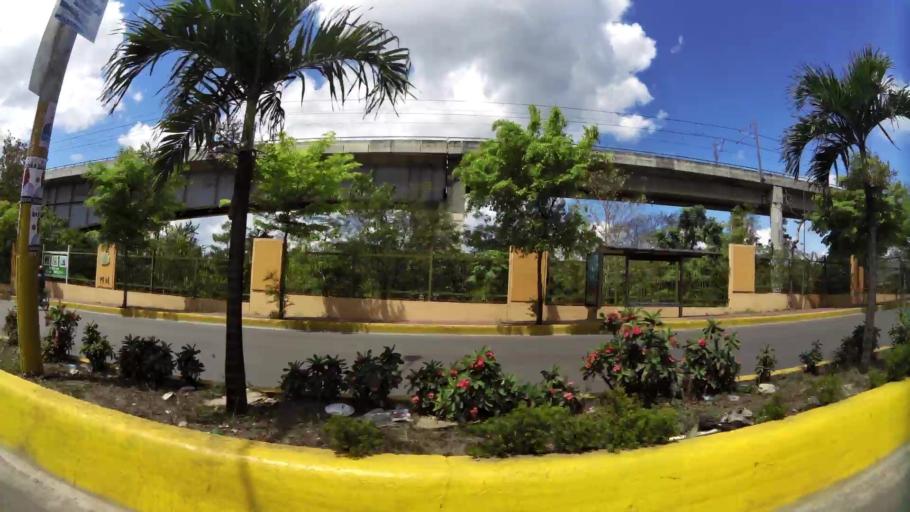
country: DO
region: Nacional
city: Ensanche Luperon
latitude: 18.5167
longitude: -69.9149
